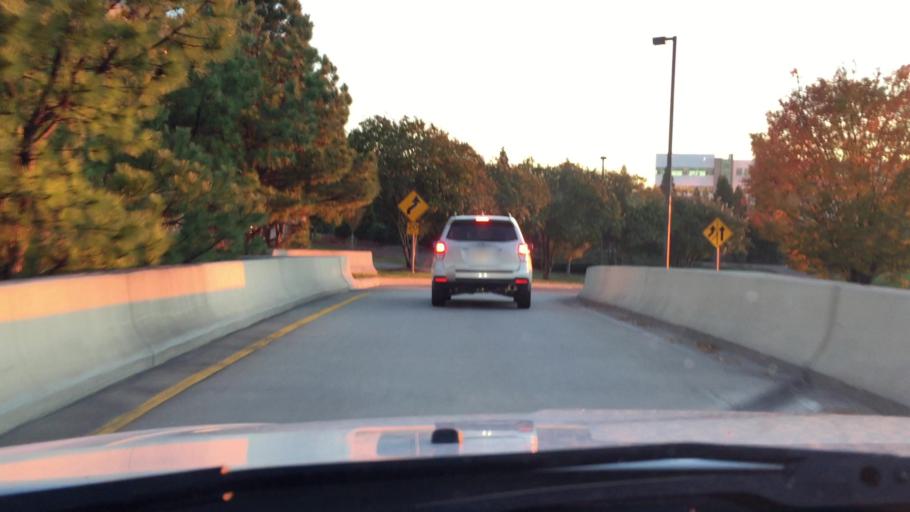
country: US
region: North Carolina
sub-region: Wake County
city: Morrisville
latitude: 35.8752
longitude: -78.7938
